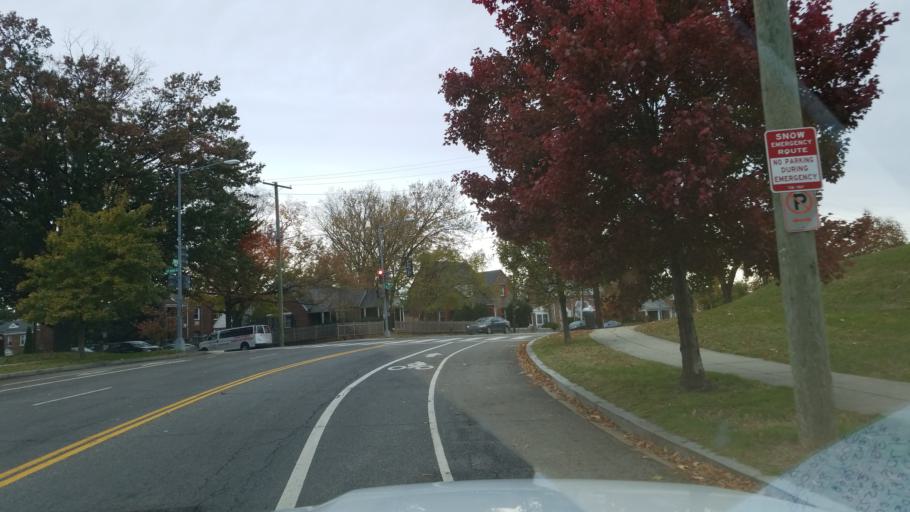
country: US
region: Maryland
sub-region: Montgomery County
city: Takoma Park
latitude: 38.9640
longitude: -77.0299
